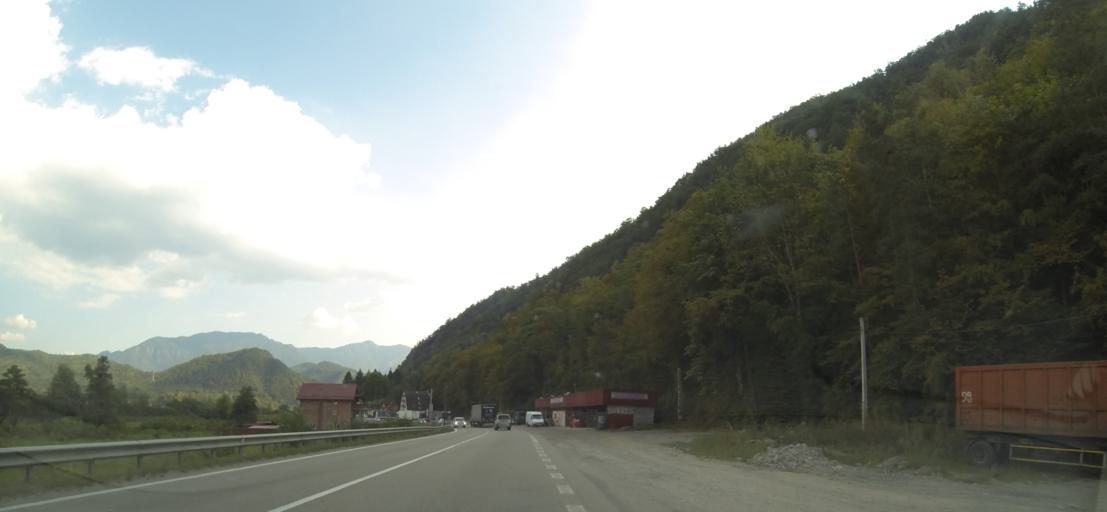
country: RO
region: Valcea
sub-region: Comuna Racovita
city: Racovita
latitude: 45.4000
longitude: 24.2985
